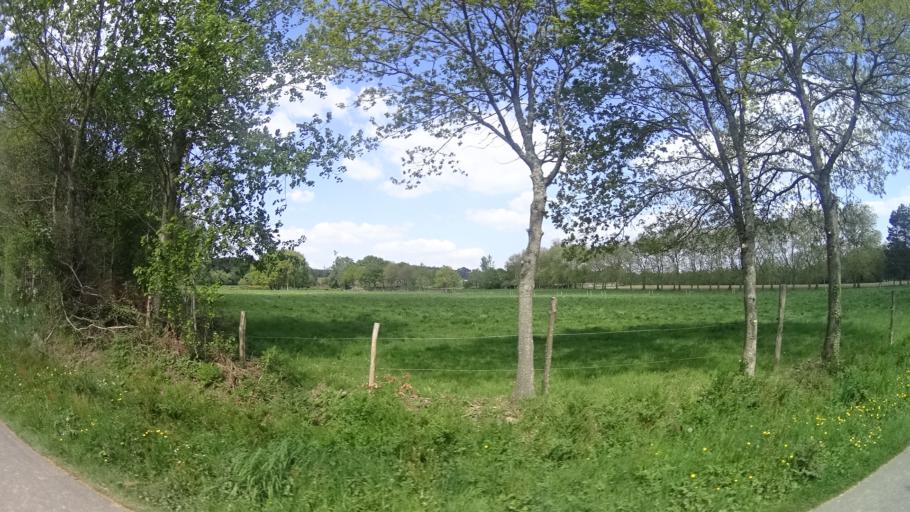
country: FR
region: Brittany
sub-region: Departement du Morbihan
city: Beganne
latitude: 47.6000
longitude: -2.1953
